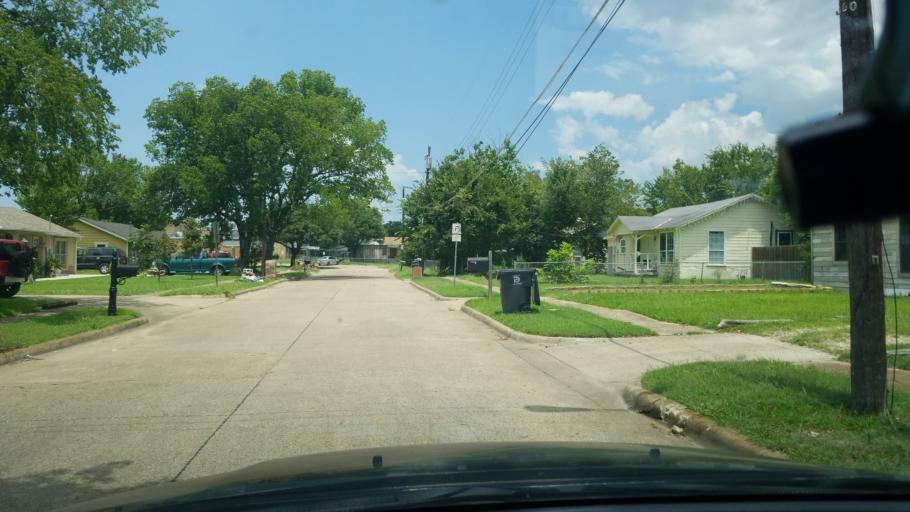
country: US
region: Texas
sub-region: Dallas County
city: Balch Springs
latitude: 32.7206
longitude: -96.6554
